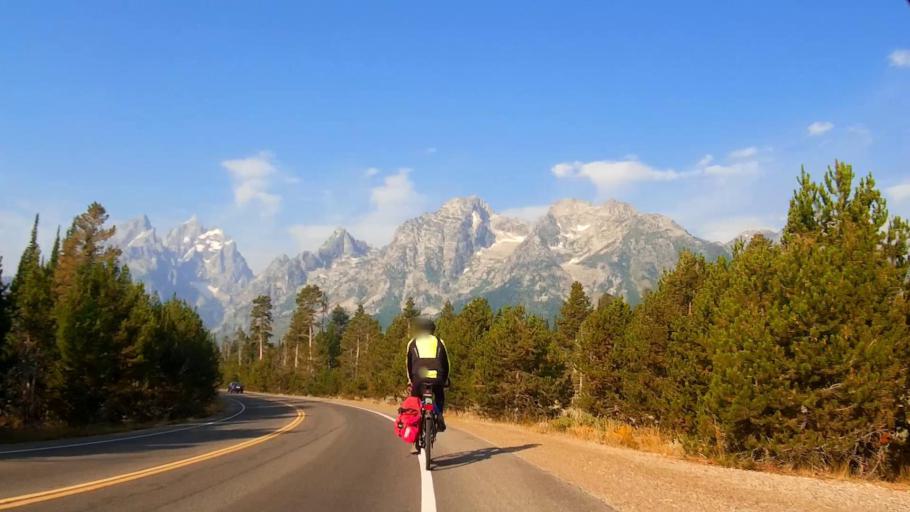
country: US
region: Wyoming
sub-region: Teton County
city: Moose Wilson Road
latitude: 43.7934
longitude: -110.7063
